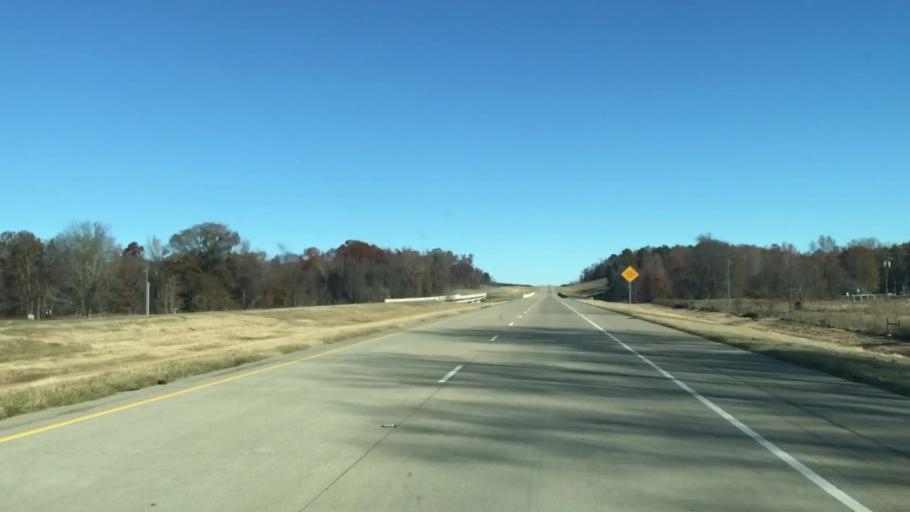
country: US
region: Louisiana
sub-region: Caddo Parish
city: Oil City
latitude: 32.7850
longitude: -93.8885
